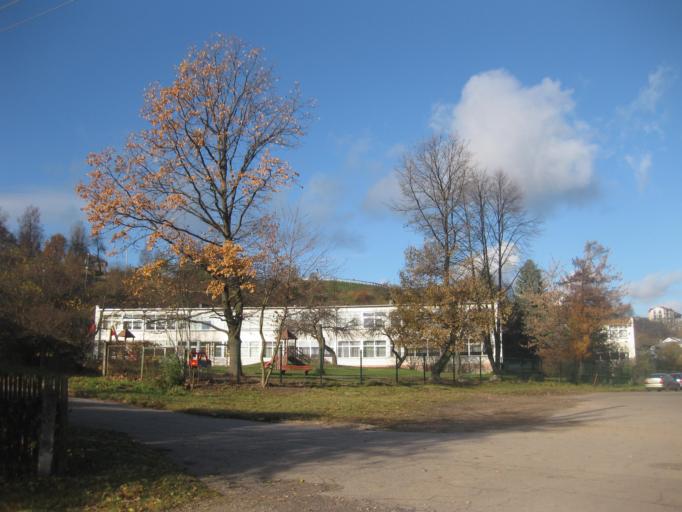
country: LT
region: Kauno apskritis
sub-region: Kaunas
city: Silainiai
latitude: 54.9197
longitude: 23.8947
